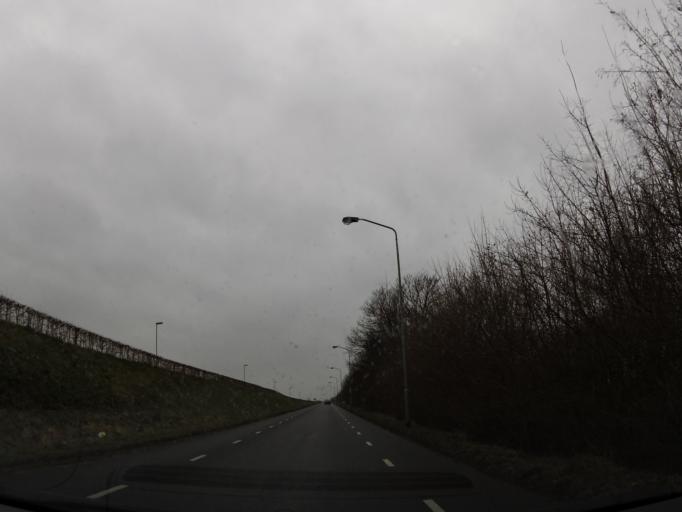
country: NL
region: Limburg
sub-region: Gemeente Maasgouw
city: Maasbracht
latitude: 51.1096
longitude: 5.8507
